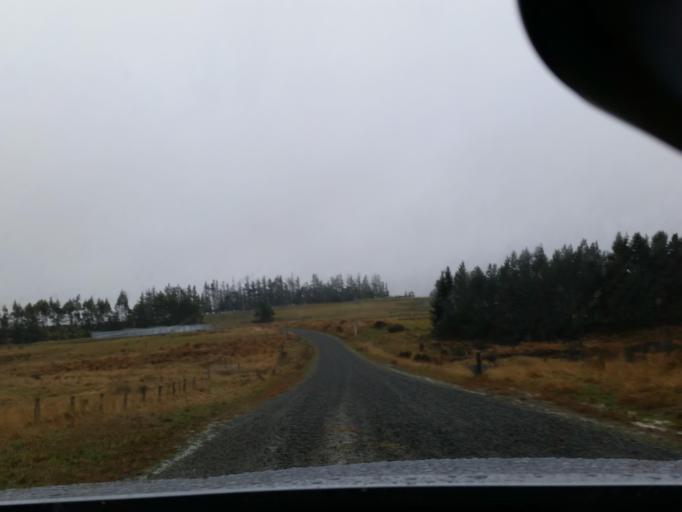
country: NZ
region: Southland
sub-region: Southland District
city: Te Anau
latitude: -45.6042
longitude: 168.0828
